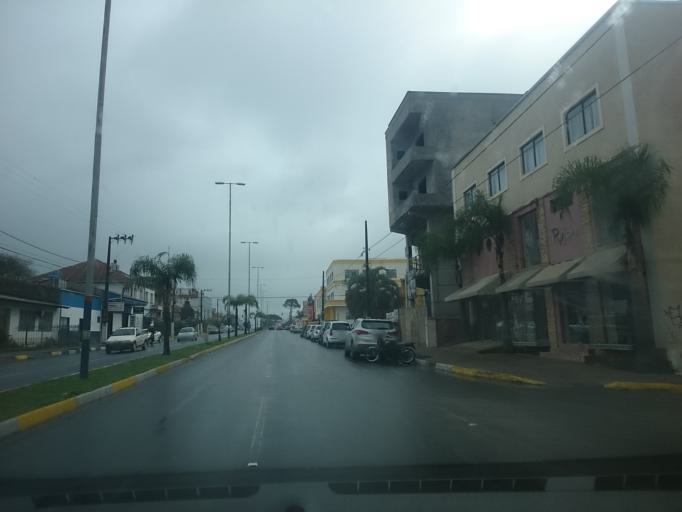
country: BR
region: Santa Catarina
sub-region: Lages
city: Lages
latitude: -27.8256
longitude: -50.3349
